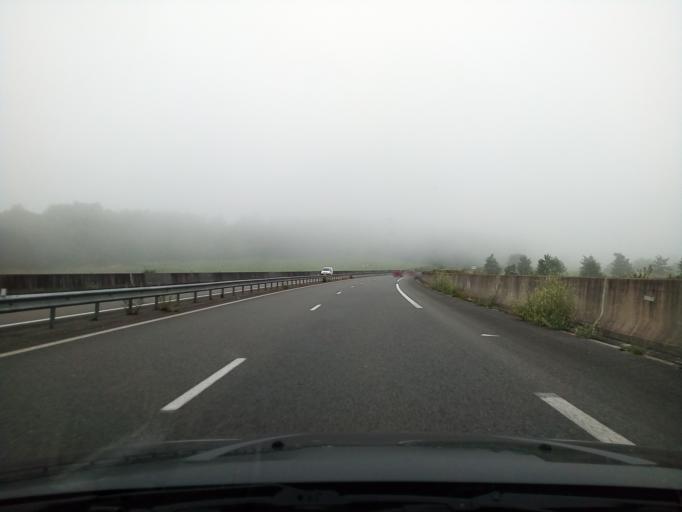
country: FR
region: Poitou-Charentes
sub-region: Departement de la Charente
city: Jarnac
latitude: 45.6665
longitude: -0.1757
